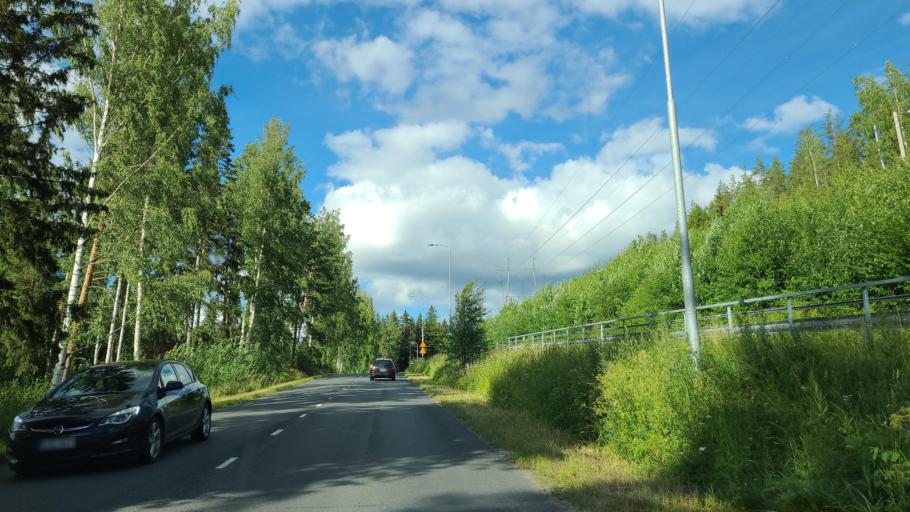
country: FI
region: Northern Savo
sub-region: Kuopio
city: Kuopio
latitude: 62.9371
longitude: 27.6365
